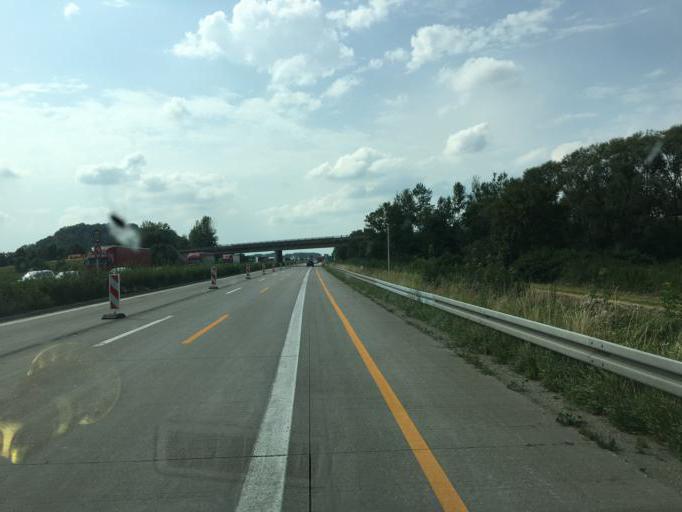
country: DE
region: Bavaria
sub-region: Lower Bavaria
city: Metten
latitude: 48.8224
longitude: 12.9289
